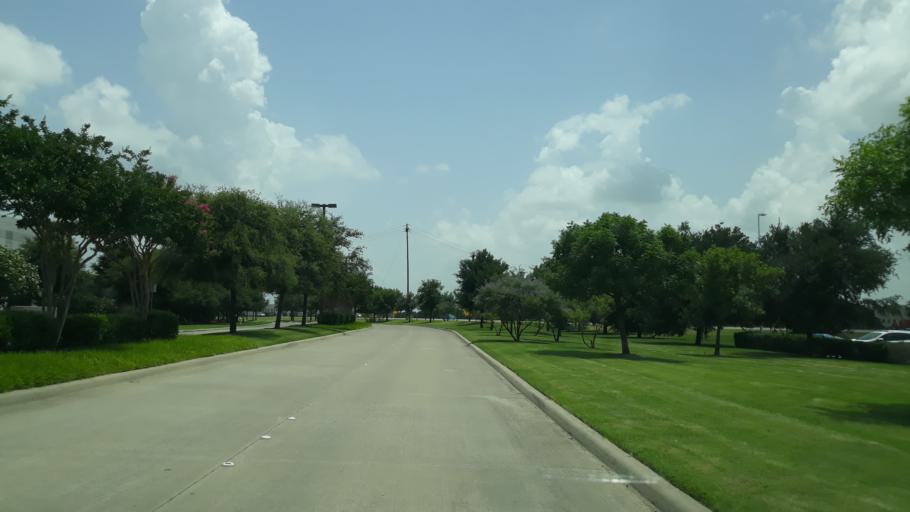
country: US
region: Texas
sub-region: Dallas County
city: Coppell
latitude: 32.9338
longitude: -97.0052
